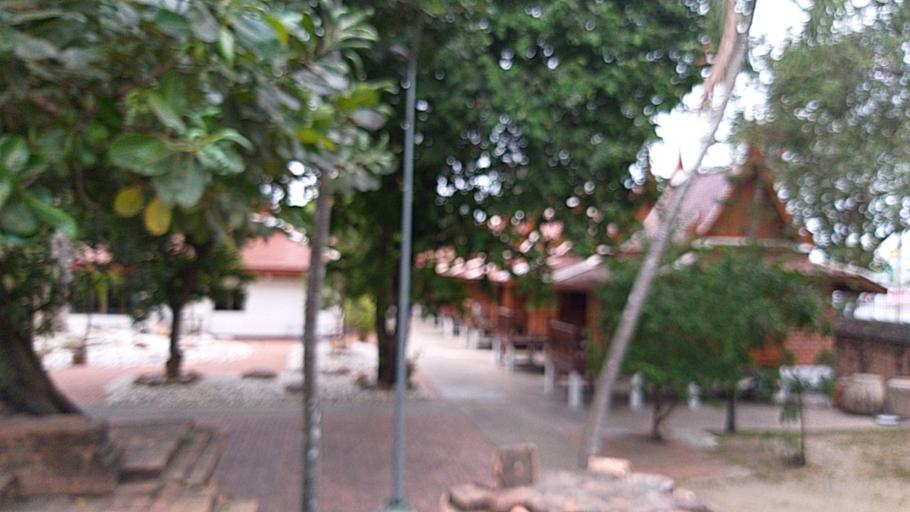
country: TH
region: Phra Nakhon Si Ayutthaya
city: Phra Nakhon Si Ayutthaya
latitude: 14.3454
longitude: 100.5917
